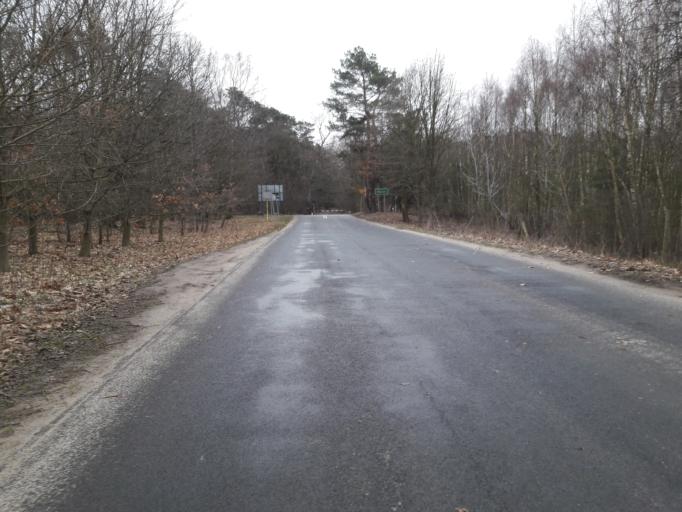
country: PL
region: Greater Poland Voivodeship
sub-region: Powiat poznanski
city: Suchy Las
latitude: 52.4872
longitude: 16.8900
